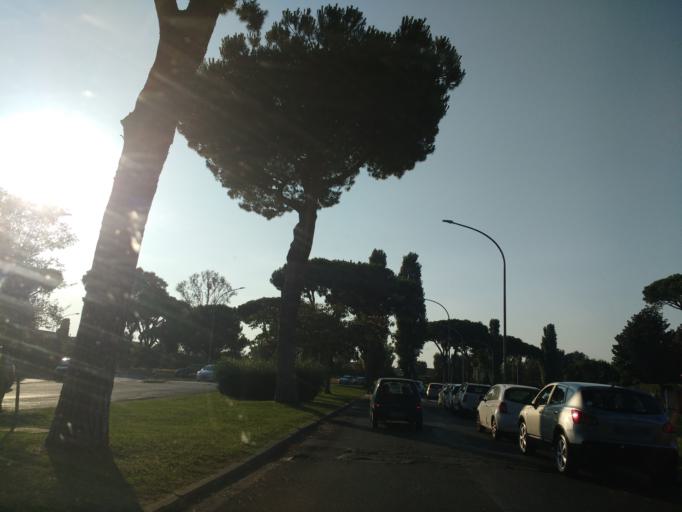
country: IT
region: Latium
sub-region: Citta metropolitana di Roma Capitale
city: Acilia-Castel Fusano-Ostia Antica
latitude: 41.7515
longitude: 12.3512
